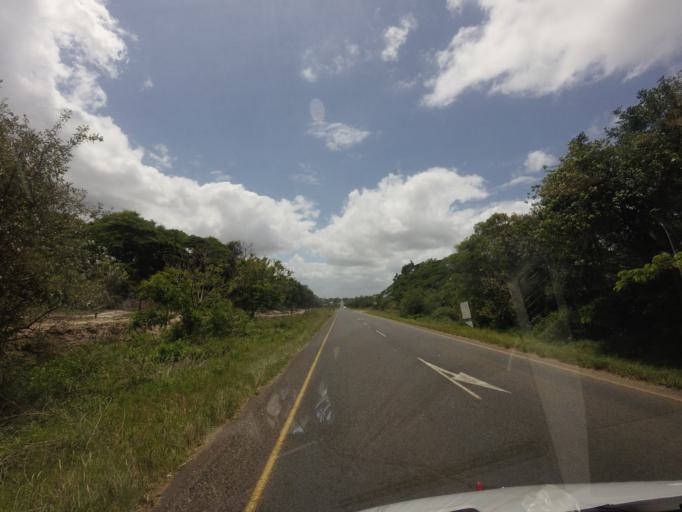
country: ZA
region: KwaZulu-Natal
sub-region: uMkhanyakude District Municipality
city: Mtubatuba
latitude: -28.3881
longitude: 32.3405
